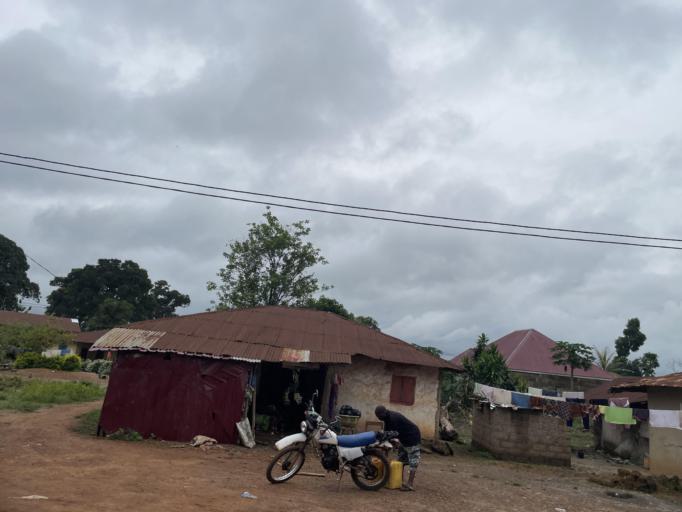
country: SL
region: Southern Province
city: Gandorhun
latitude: 7.4358
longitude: -11.8428
